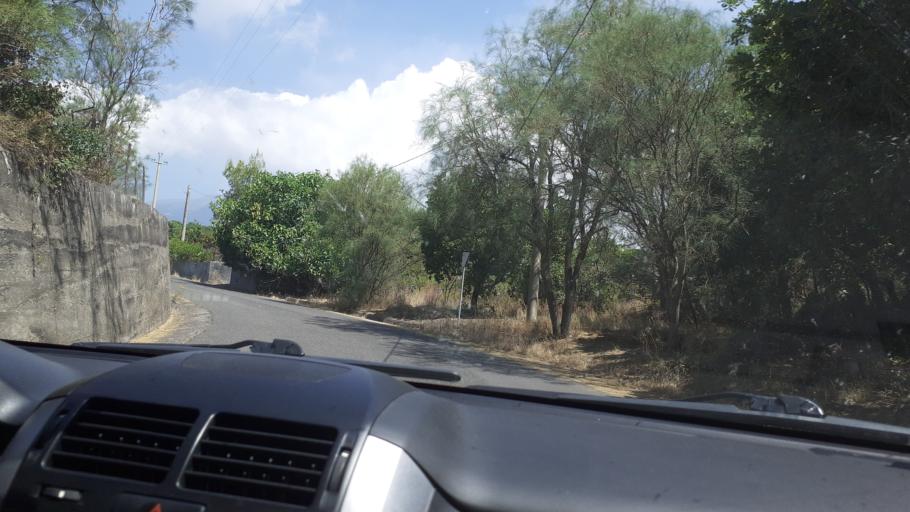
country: IT
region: Sicily
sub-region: Catania
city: Nicolosi
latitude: 37.6351
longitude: 15.0245
